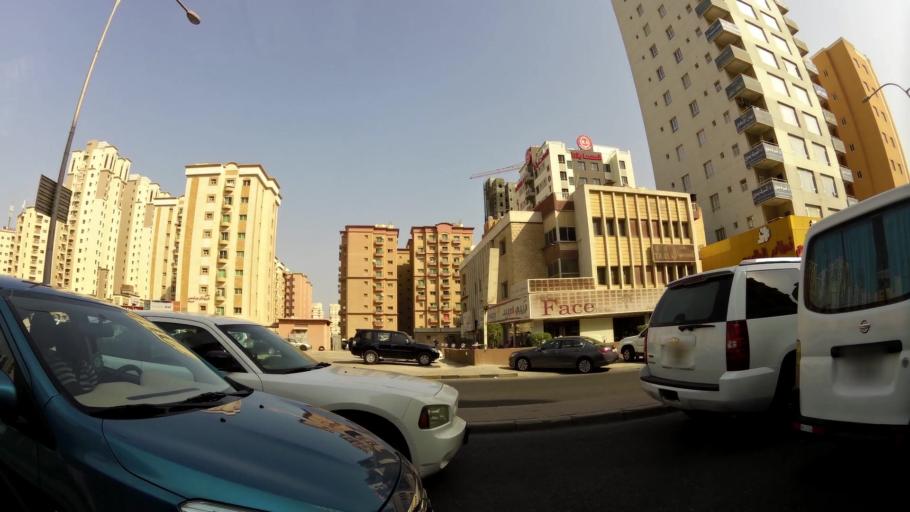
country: KW
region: Muhafazat Hawalli
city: As Salimiyah
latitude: 29.3356
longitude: 48.0536
